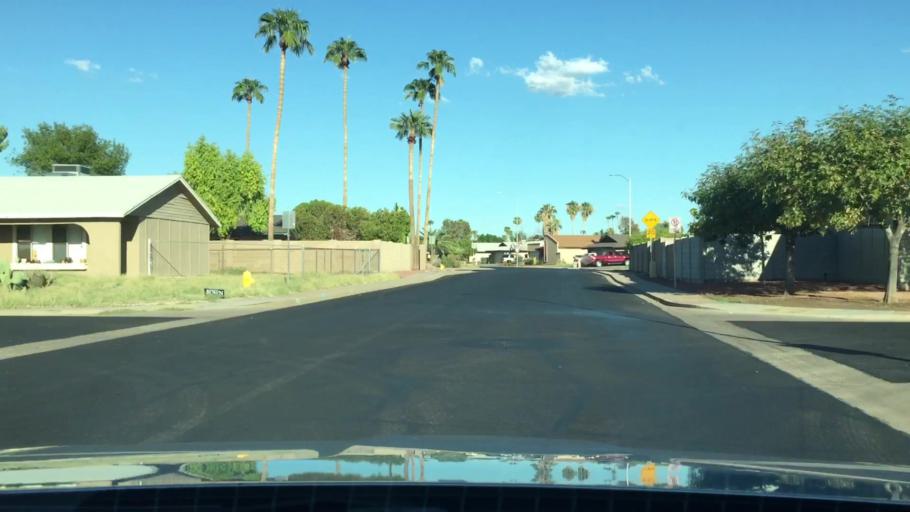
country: US
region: Arizona
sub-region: Maricopa County
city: San Carlos
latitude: 33.3595
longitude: -111.8683
